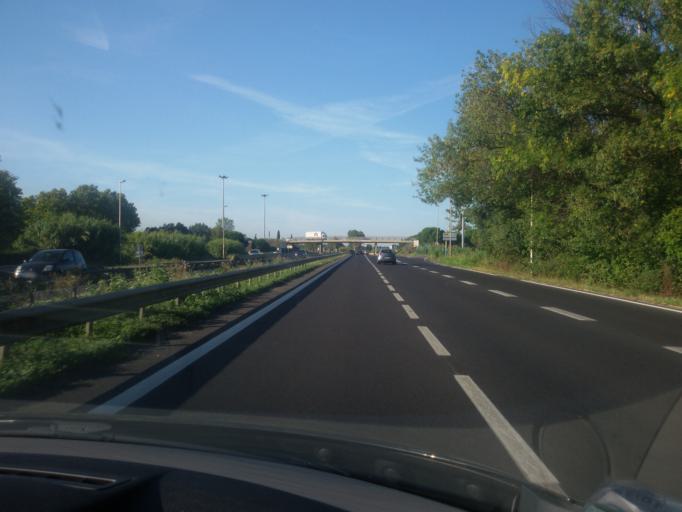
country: FR
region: Languedoc-Roussillon
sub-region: Departement de l'Herault
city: Lattes
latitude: 43.5691
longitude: 3.8957
